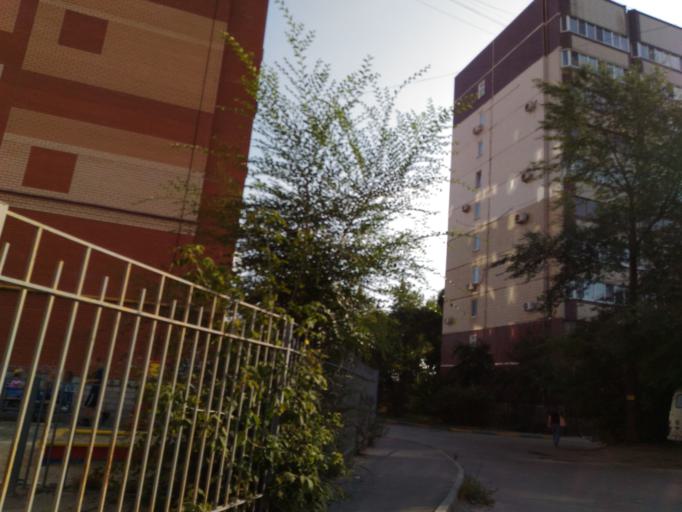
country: RU
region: Ulyanovsk
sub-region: Ulyanovskiy Rayon
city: Ulyanovsk
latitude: 54.3331
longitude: 48.3899
